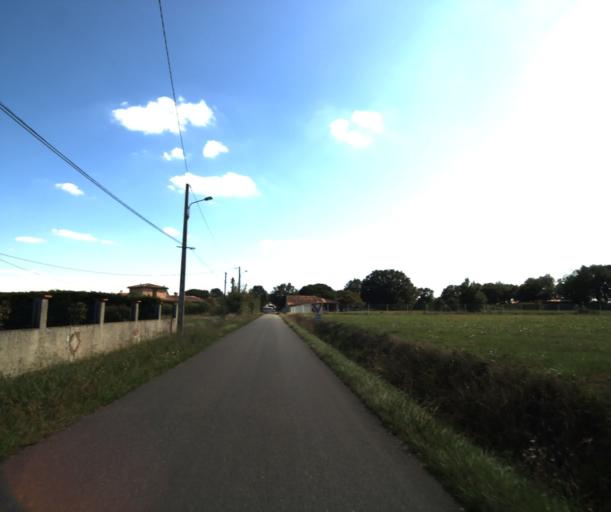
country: FR
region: Midi-Pyrenees
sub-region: Departement de la Haute-Garonne
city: Saint-Lys
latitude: 43.5051
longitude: 1.2077
